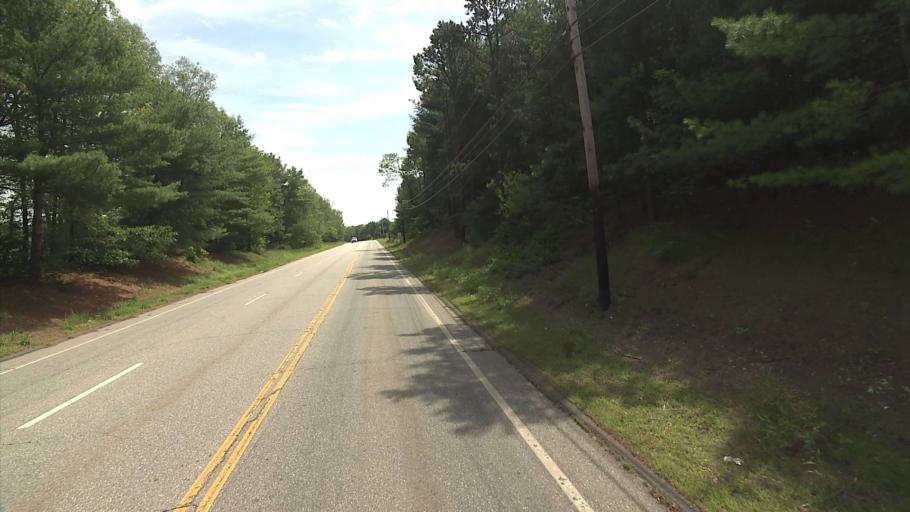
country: US
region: Connecticut
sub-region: Windham County
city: Willimantic
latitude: 41.7315
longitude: -72.2139
